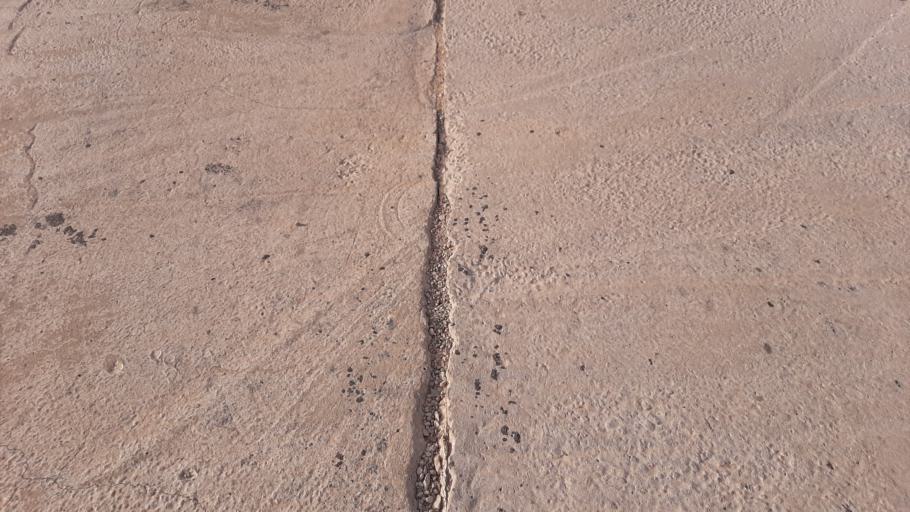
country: TN
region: Safaqis
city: Bi'r `Ali Bin Khalifah
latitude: 34.5410
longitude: 10.1981
